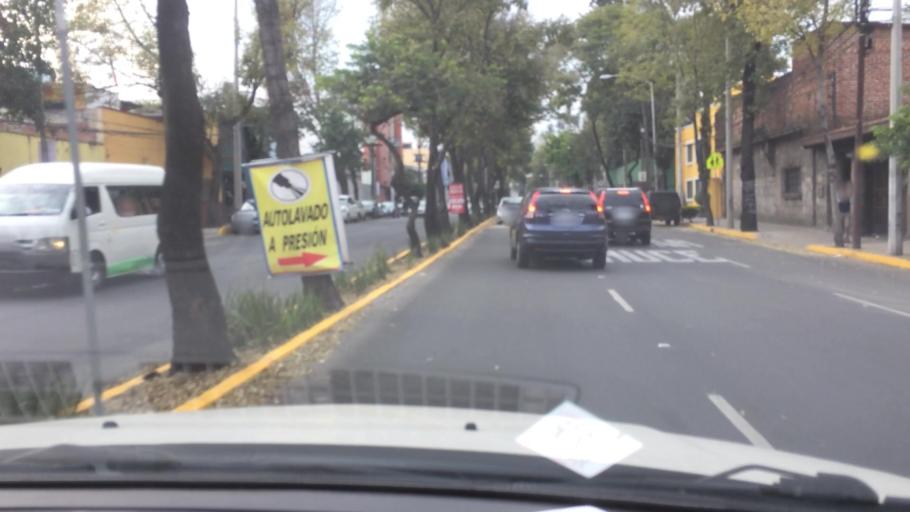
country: MX
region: Mexico City
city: Tlalpan
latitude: 19.2944
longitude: -99.1734
